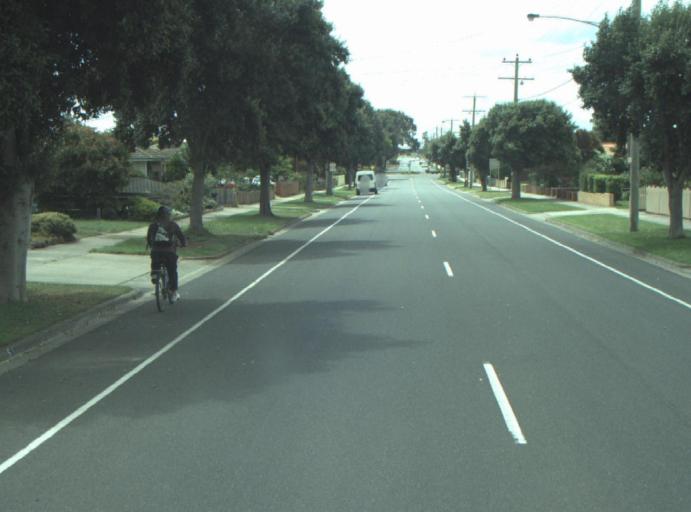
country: AU
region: Victoria
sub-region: Greater Geelong
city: Bell Park
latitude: -38.0697
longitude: 144.3669
